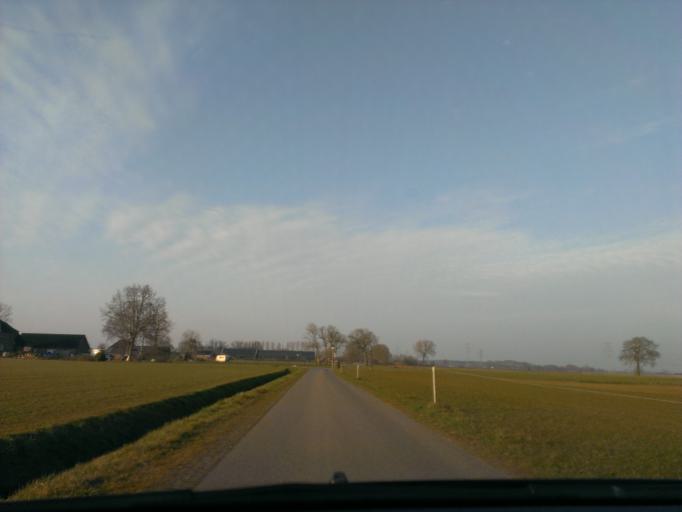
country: NL
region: Gelderland
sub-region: Gemeente Epe
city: Oene
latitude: 52.3424
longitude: 6.0577
